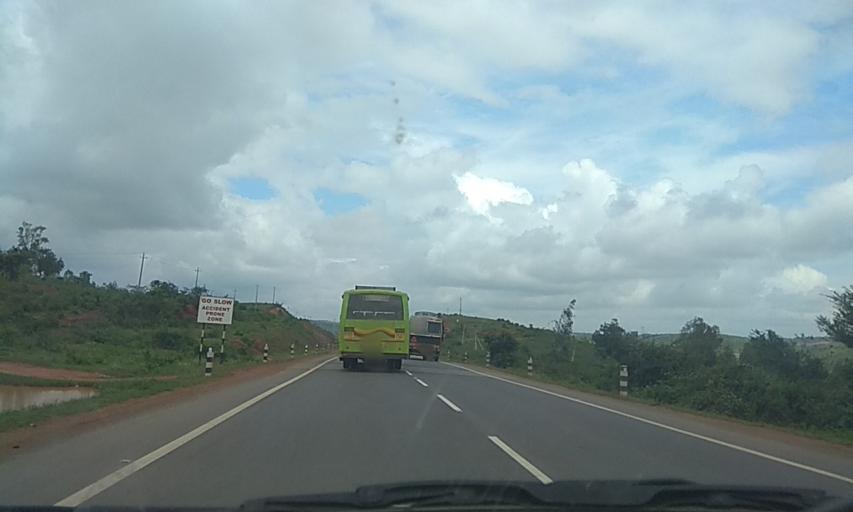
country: IN
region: Karnataka
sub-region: Dharwad
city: Hubli
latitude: 15.4008
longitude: 74.9984
